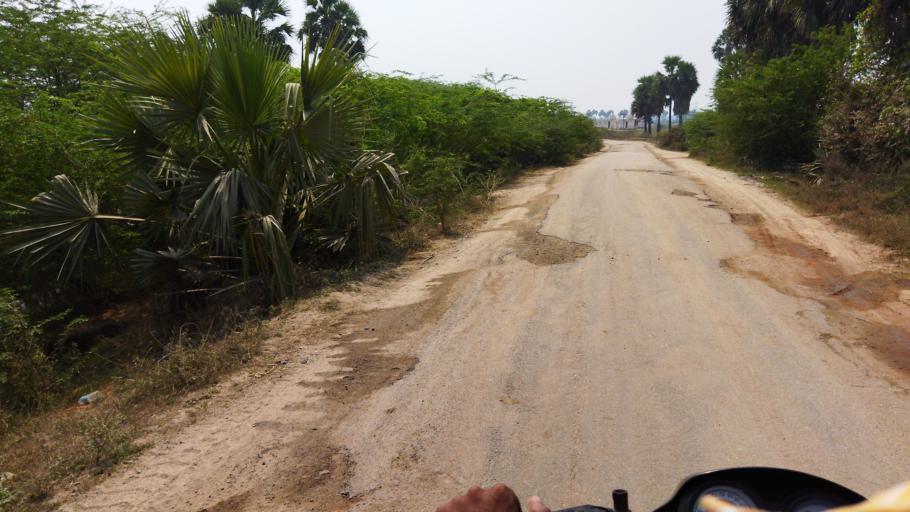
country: IN
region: Telangana
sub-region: Nalgonda
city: Nalgonda
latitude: 17.1400
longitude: 79.3863
